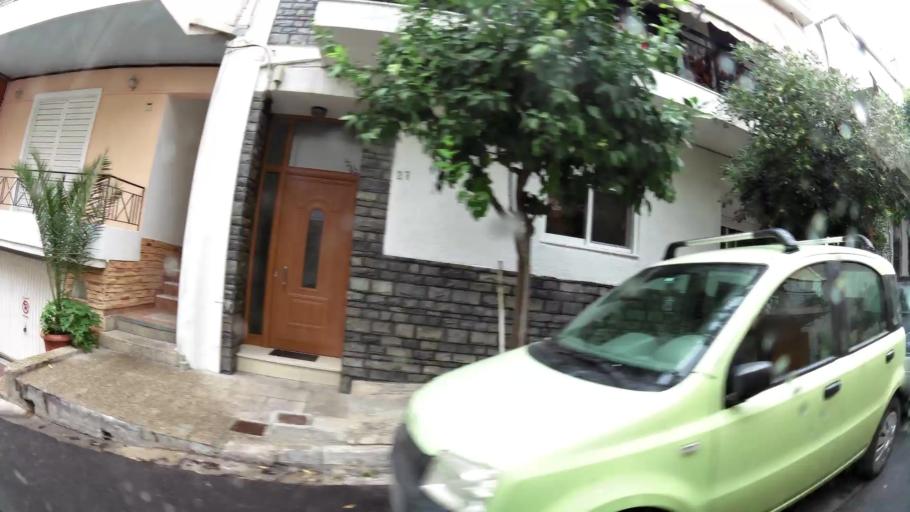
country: GR
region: Attica
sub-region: Nomos Piraios
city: Korydallos
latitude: 37.9964
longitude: 23.6440
